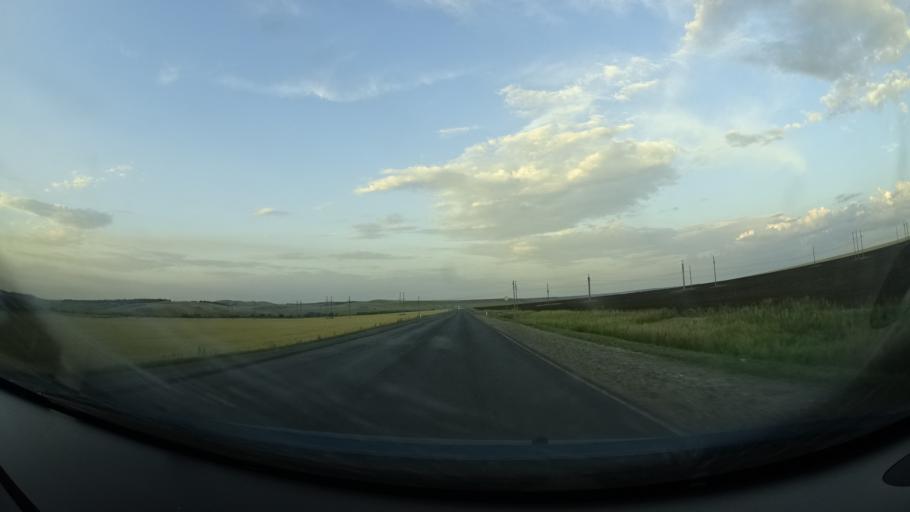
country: RU
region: Orenburg
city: Severnoye
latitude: 54.1255
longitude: 52.5637
